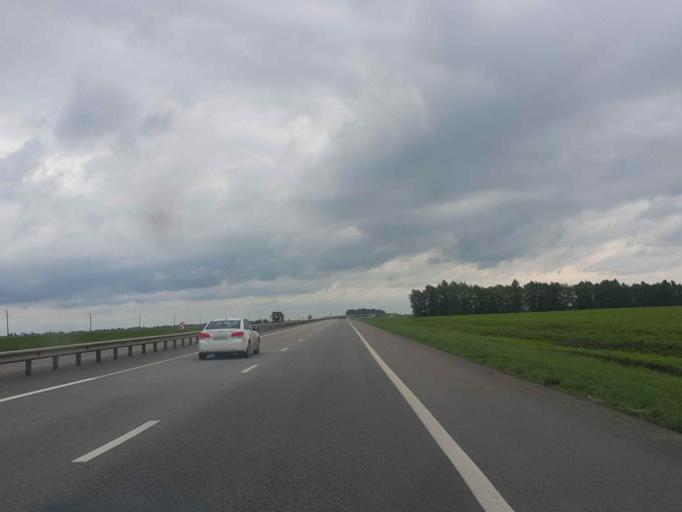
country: RU
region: Tambov
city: Zavoronezhskoye
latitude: 52.8298
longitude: 40.8918
